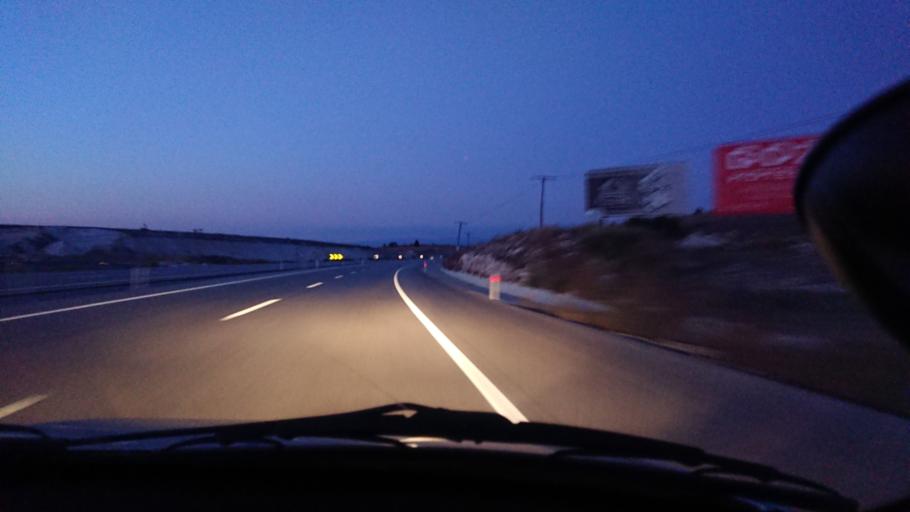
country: TR
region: Kuetahya
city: Cavdarhisar
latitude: 39.1660
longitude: 29.5942
